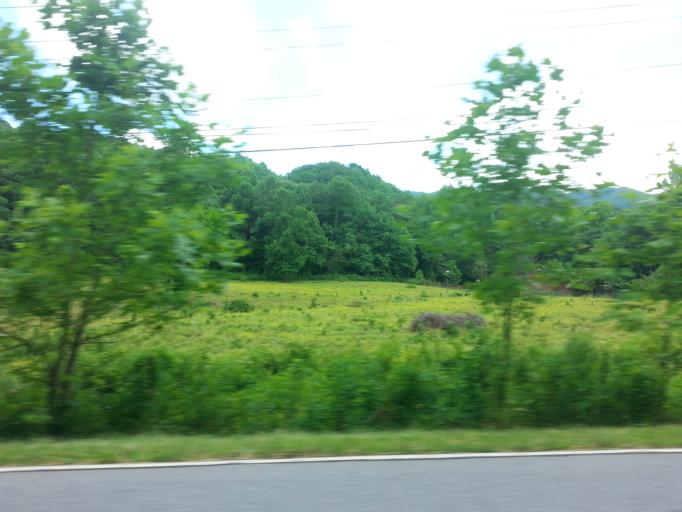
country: US
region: North Carolina
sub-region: Cherokee County
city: Andrews
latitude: 35.2118
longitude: -83.7587
